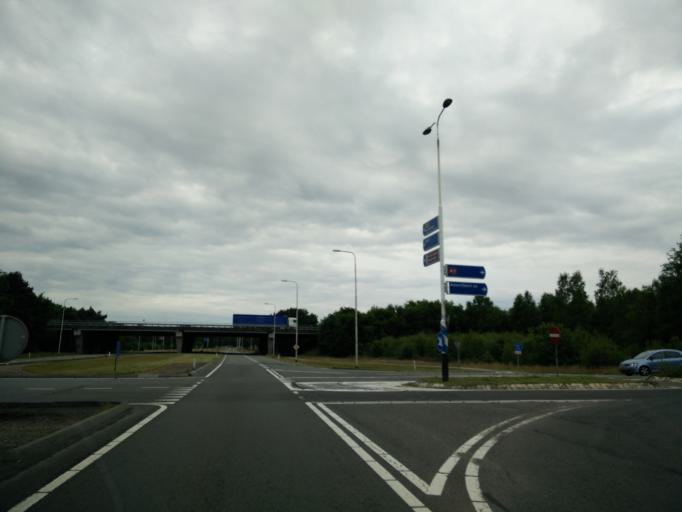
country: NL
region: Gelderland
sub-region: Gemeente Apeldoorn
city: Beekbergen
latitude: 52.1835
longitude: 5.9156
